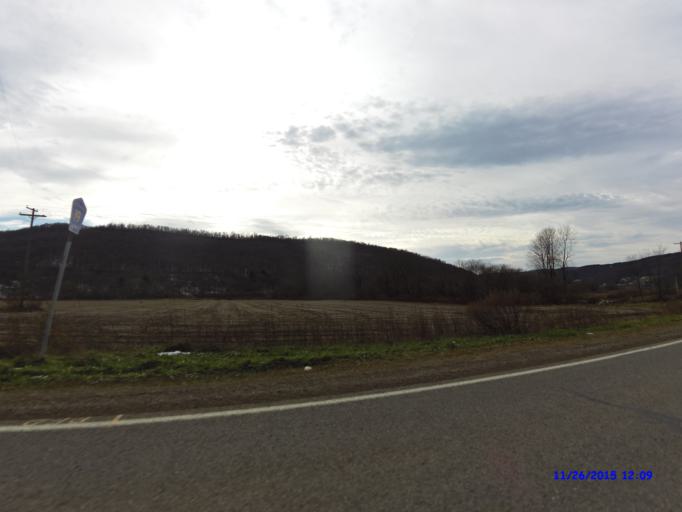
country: US
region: New York
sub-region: Cattaraugus County
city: Allegany
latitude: 42.1936
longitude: -78.4794
